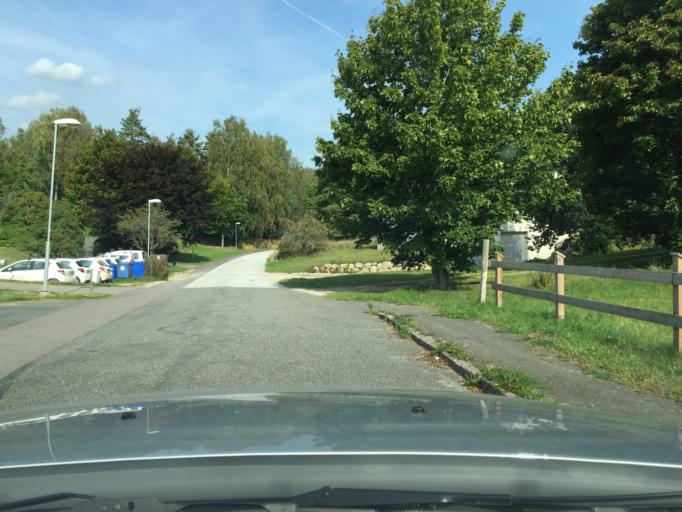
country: SE
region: Skane
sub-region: Kristianstads Kommun
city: Degeberga
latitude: 55.7263
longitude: 14.1002
